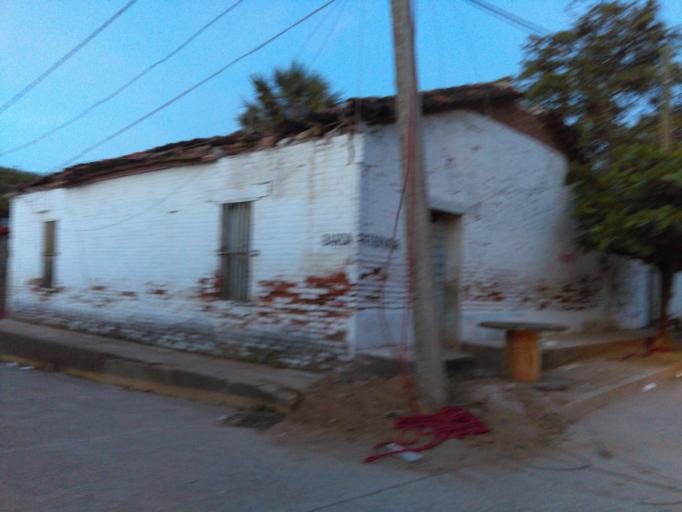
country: MX
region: Oaxaca
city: San Jeronimo Ixtepec
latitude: 16.5687
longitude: -95.0977
